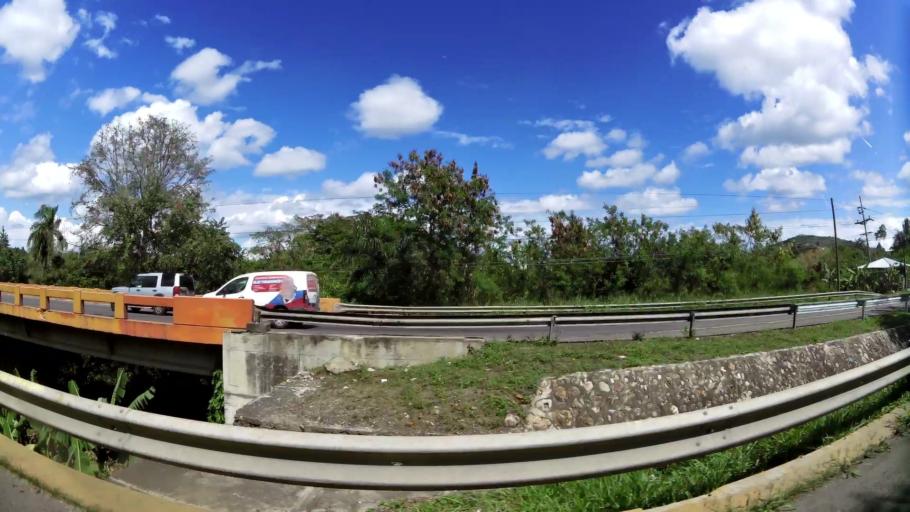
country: DO
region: La Vega
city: Rio Verde Arriba
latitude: 19.3148
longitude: -70.5864
